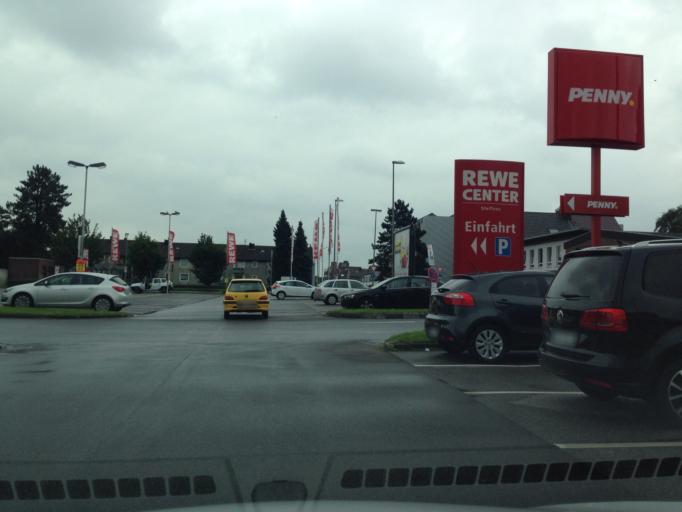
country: DE
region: North Rhine-Westphalia
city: Erkelenz
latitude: 51.0747
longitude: 6.3057
